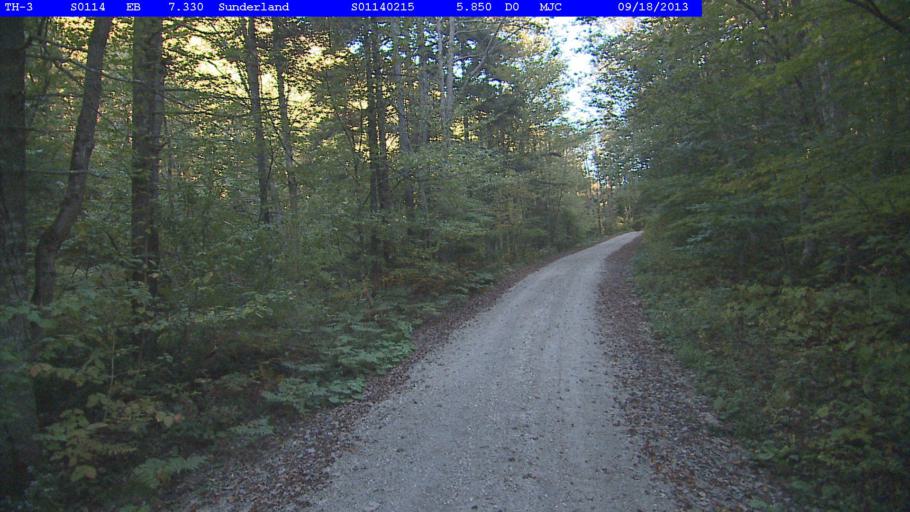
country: US
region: Vermont
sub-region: Bennington County
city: Arlington
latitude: 43.0593
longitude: -73.0688
